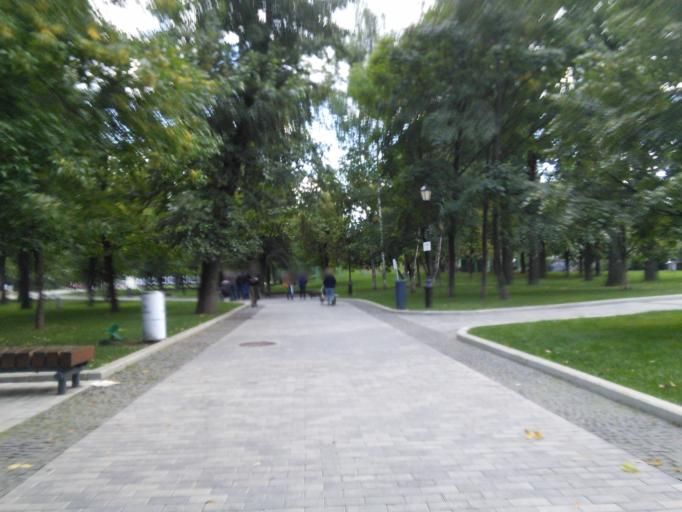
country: RU
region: Moscow
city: Sokol'niki
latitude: 55.7686
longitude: 37.6591
